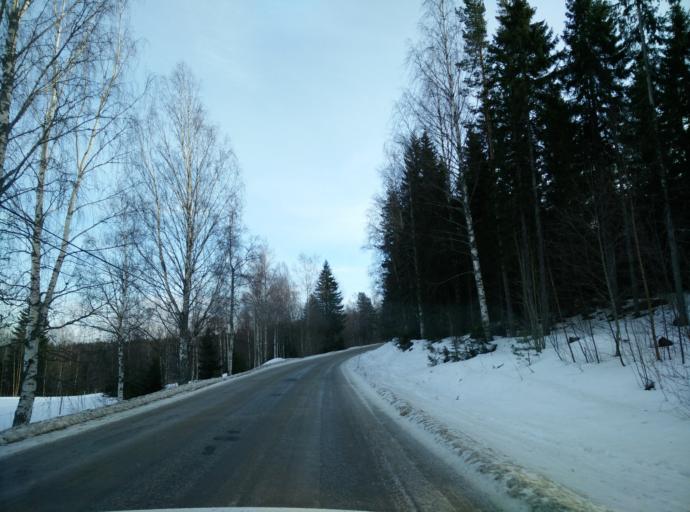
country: SE
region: Vaesternorrland
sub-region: Sundsvalls Kommun
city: Njurundabommen
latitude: 62.2015
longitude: 17.2756
